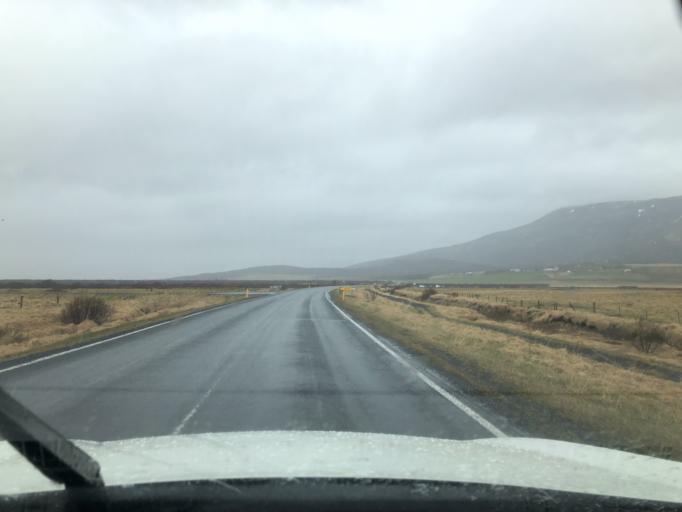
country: IS
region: South
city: Selfoss
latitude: 64.2402
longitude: -20.5147
